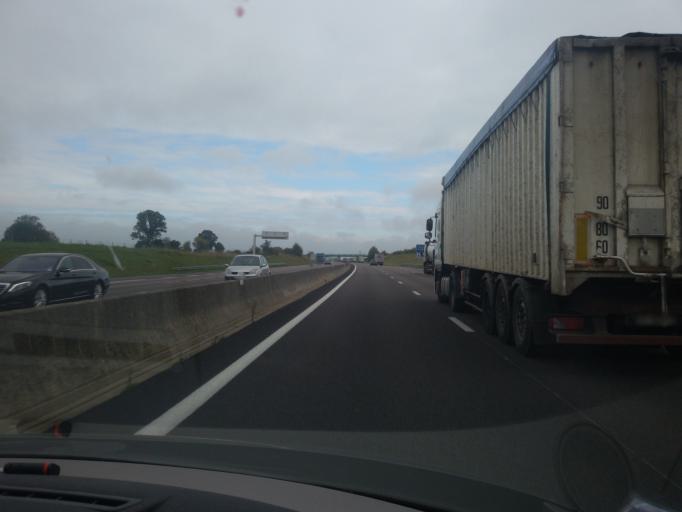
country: FR
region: Haute-Normandie
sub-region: Departement de l'Eure
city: Hauville
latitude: 49.3703
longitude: 0.7125
